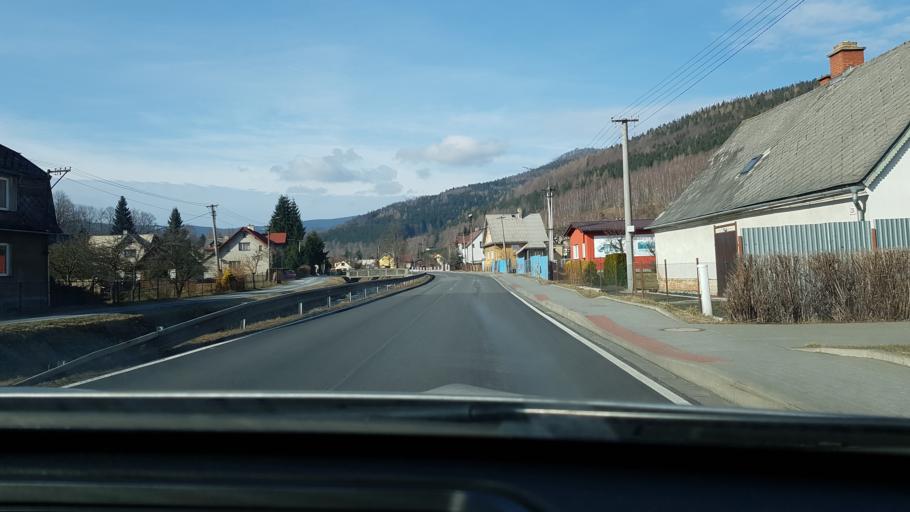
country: CZ
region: Olomoucky
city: Vapenna
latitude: 50.2265
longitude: 17.1270
